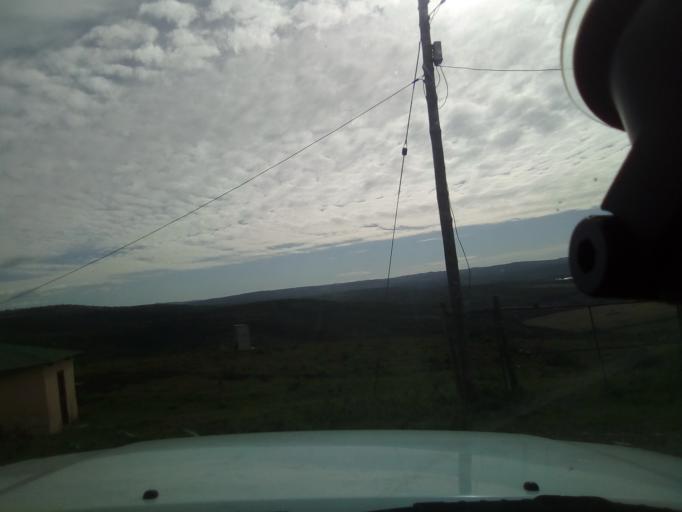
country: ZA
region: Eastern Cape
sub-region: Amathole District Municipality
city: Komga
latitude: -32.7905
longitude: 27.9623
